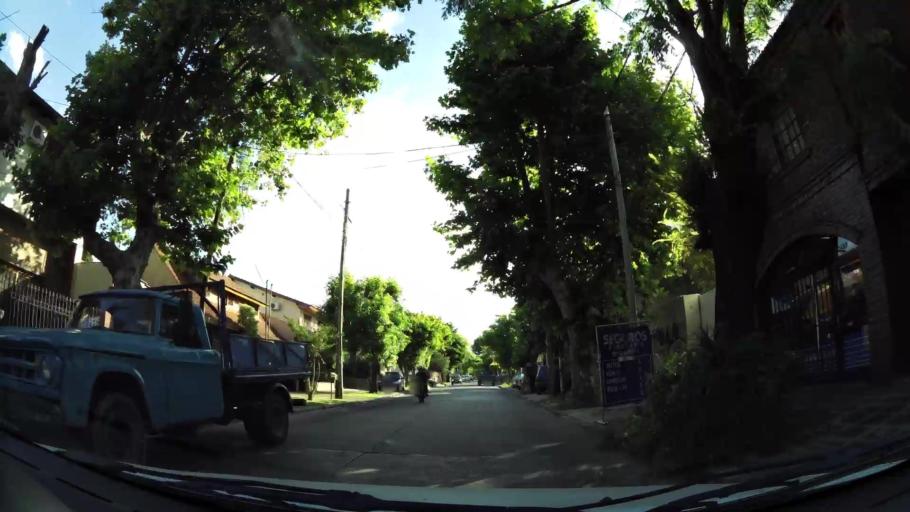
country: AR
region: Buenos Aires
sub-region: Partido de General San Martin
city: General San Martin
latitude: -34.5385
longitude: -58.5636
